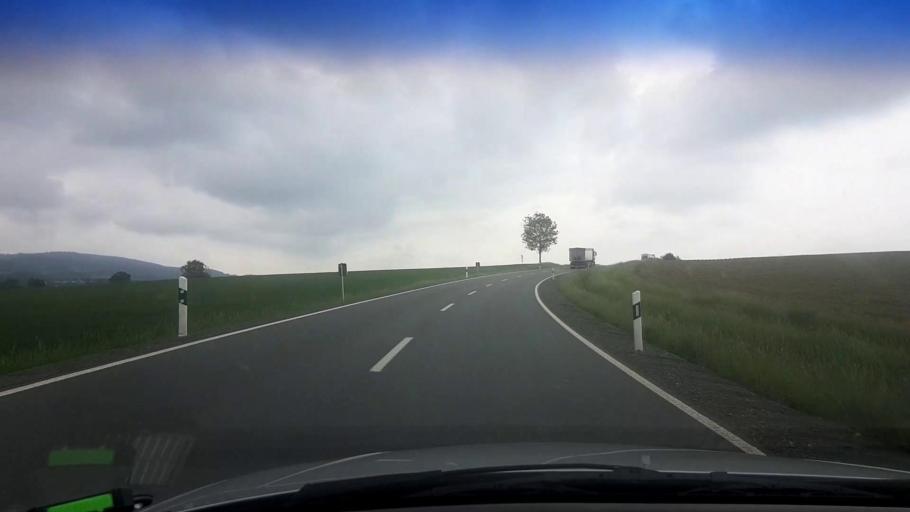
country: DE
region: Bavaria
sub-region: Upper Franconia
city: Gesees
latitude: 50.0224
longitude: 11.6641
